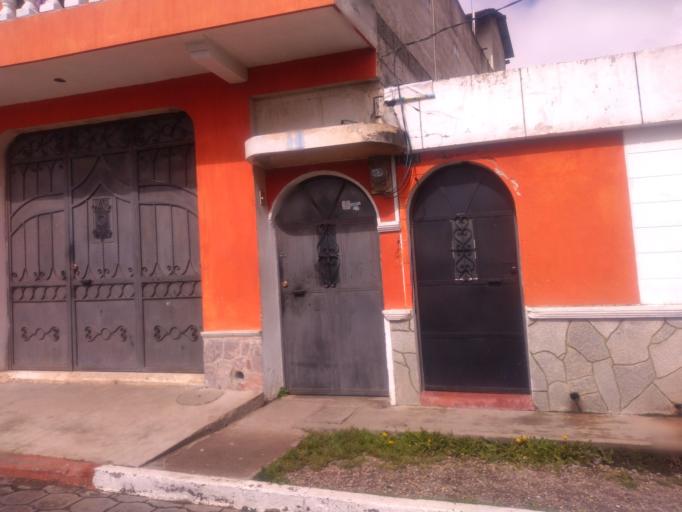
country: GT
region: Quetzaltenango
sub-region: Municipio de La Esperanza
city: La Esperanza
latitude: 14.8659
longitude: -91.5657
